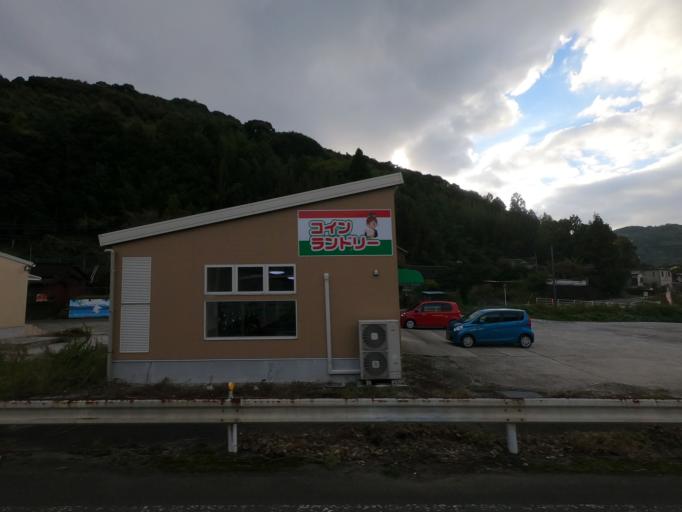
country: JP
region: Kumamoto
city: Minamata
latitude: 32.2677
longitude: 130.5054
